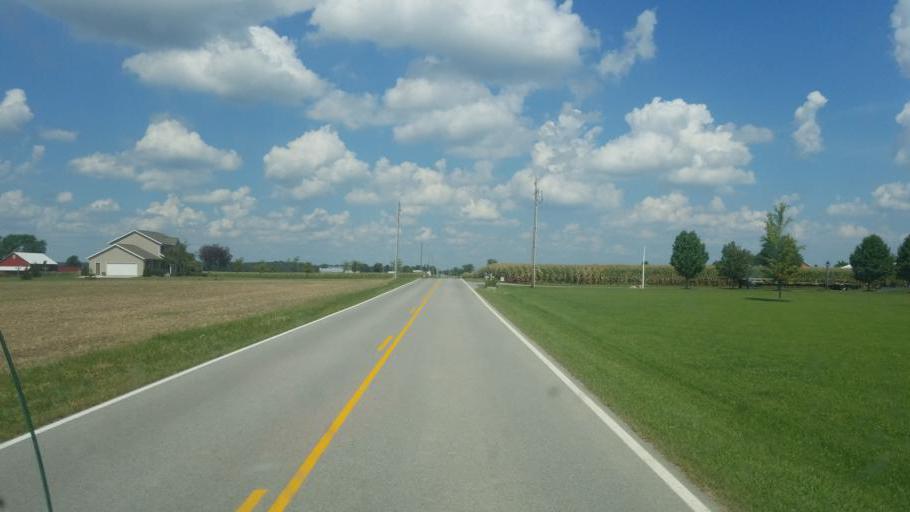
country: US
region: Ohio
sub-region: Hancock County
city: Arlington
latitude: 40.8731
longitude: -83.7273
